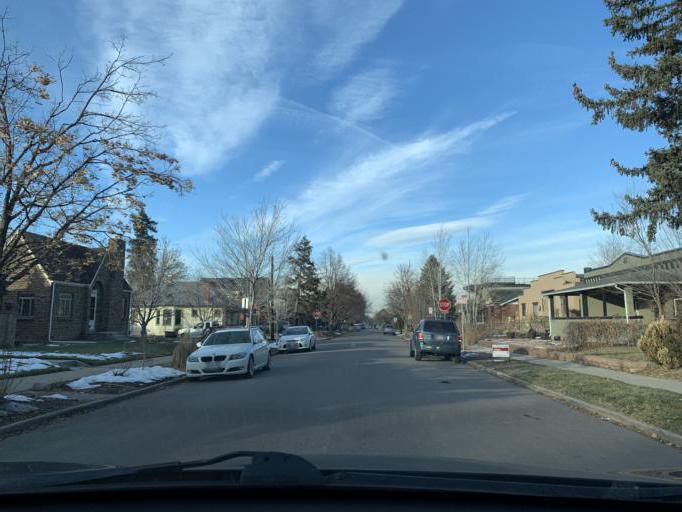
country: US
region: Colorado
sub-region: Jefferson County
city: Edgewater
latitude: 39.7720
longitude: -105.0393
